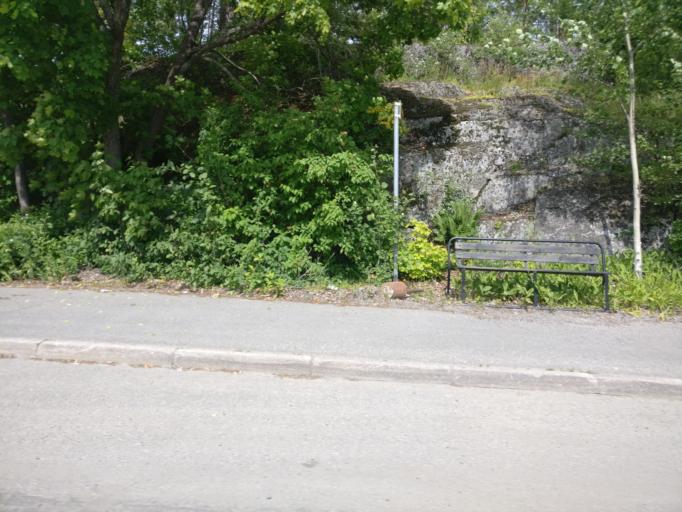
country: FI
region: Southern Savonia
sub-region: Savonlinna
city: Savonlinna
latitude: 61.8698
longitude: 28.9226
